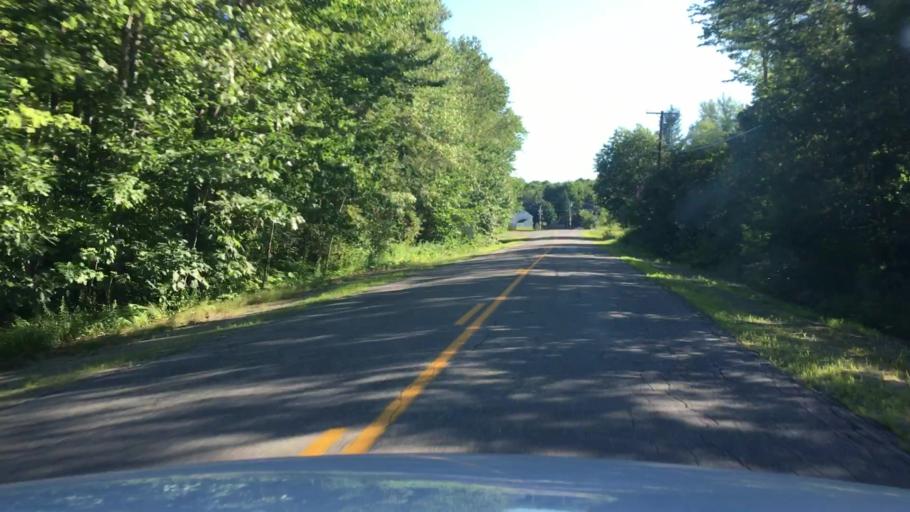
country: US
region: Maine
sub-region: Penobscot County
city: Howland
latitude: 45.1872
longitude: -68.6123
